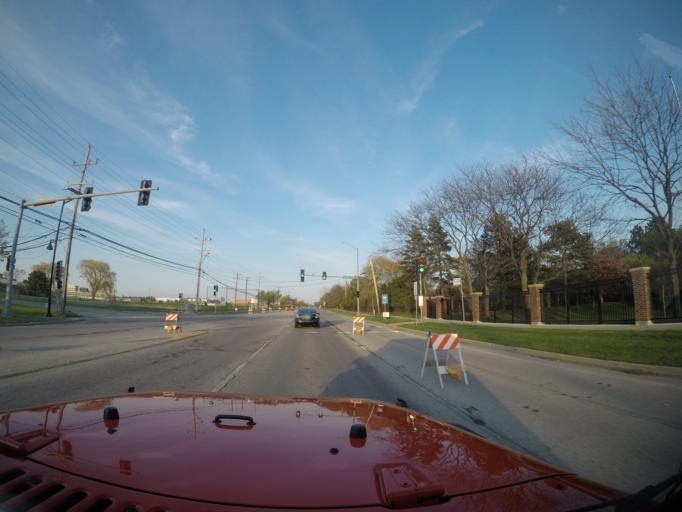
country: US
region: Illinois
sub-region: Cook County
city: Northbrook
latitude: 42.0875
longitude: -87.8594
